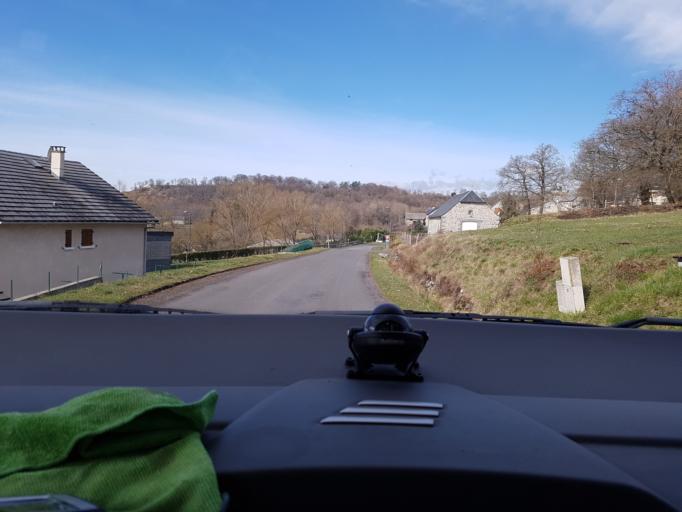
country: FR
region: Auvergne
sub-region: Departement du Cantal
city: Saint-Flour
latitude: 45.0021
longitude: 3.0249
